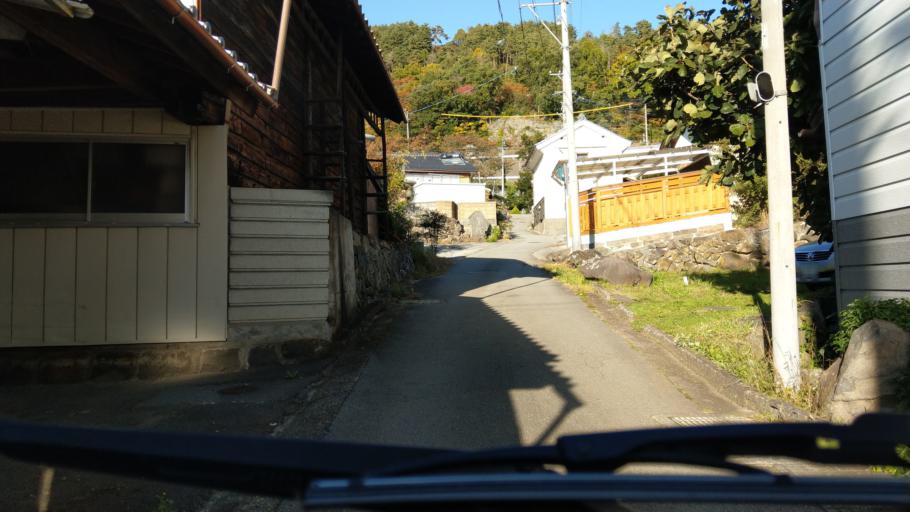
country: JP
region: Nagano
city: Komoro
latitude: 36.3408
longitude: 138.4171
